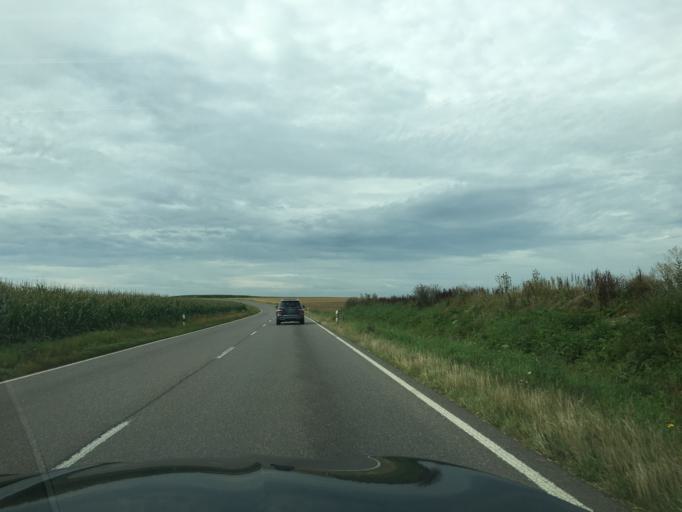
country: DE
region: Baden-Wuerttemberg
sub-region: Tuebingen Region
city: Emeringen
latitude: 48.2126
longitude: 9.5337
